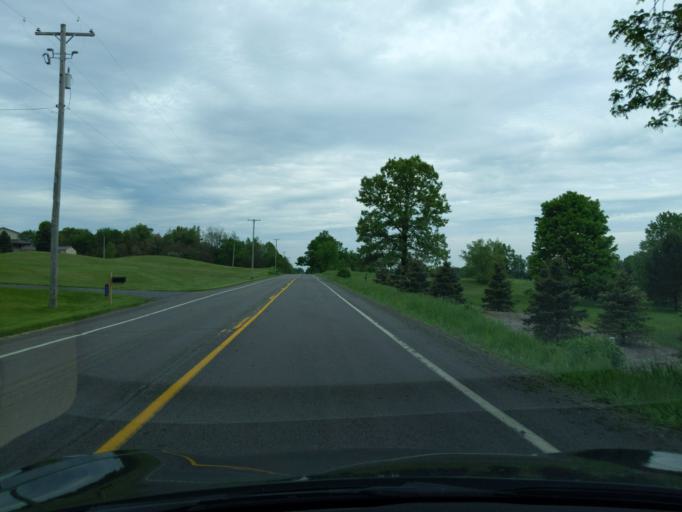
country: US
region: Michigan
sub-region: Ingham County
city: Mason
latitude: 42.5661
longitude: -84.3569
